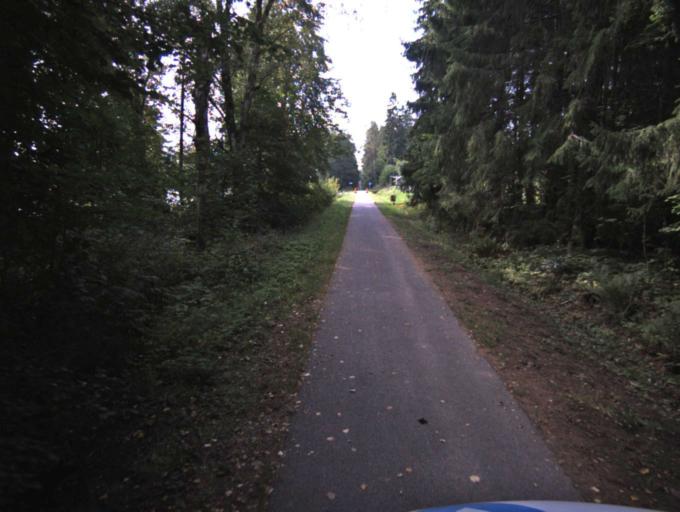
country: SE
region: Vaestra Goetaland
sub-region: Ulricehamns Kommun
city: Ulricehamn
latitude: 57.6689
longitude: 13.3679
